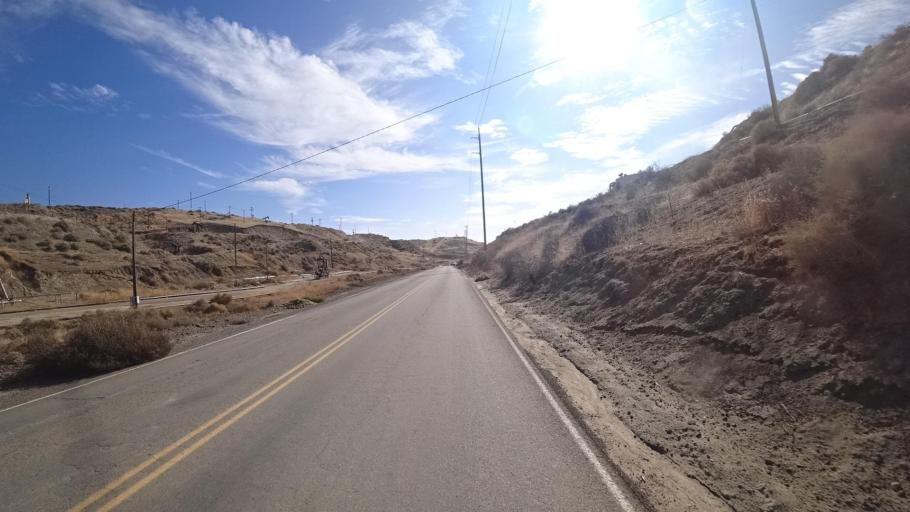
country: US
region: California
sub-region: Kern County
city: Oildale
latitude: 35.5828
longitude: -118.9593
